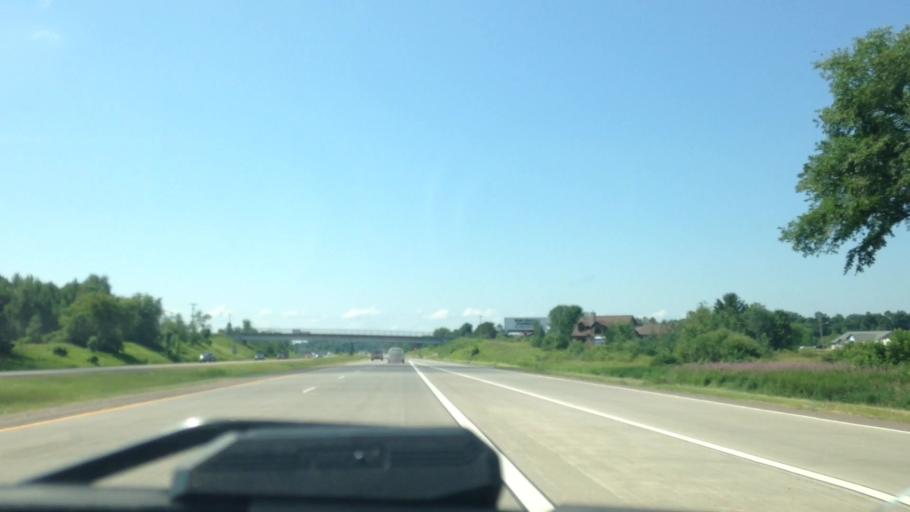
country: US
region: Wisconsin
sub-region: Barron County
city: Rice Lake
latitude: 45.5053
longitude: -91.7633
